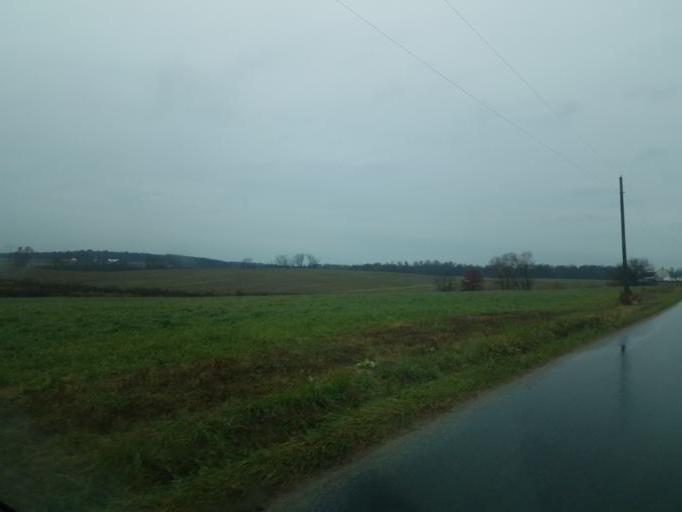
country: US
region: Ohio
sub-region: Knox County
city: Fredericktown
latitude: 40.5389
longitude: -82.5887
